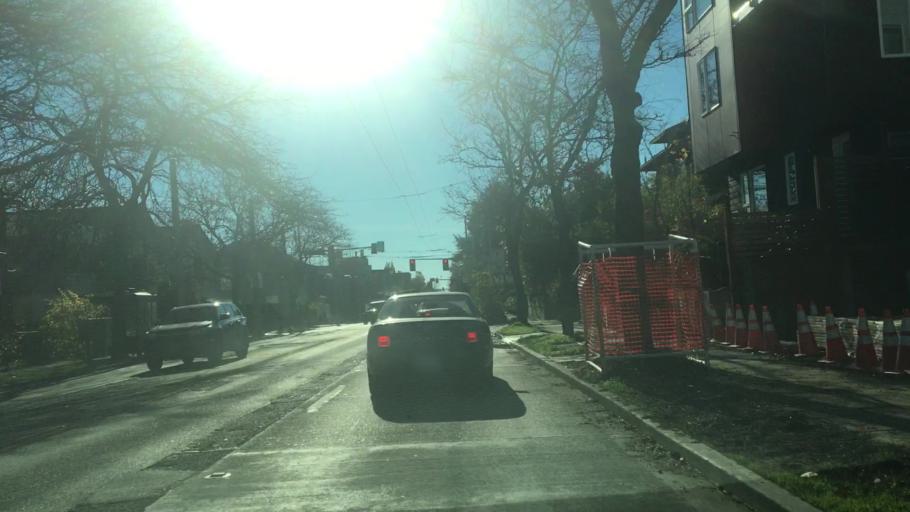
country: US
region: Washington
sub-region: King County
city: Seattle
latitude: 47.6210
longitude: -122.3026
